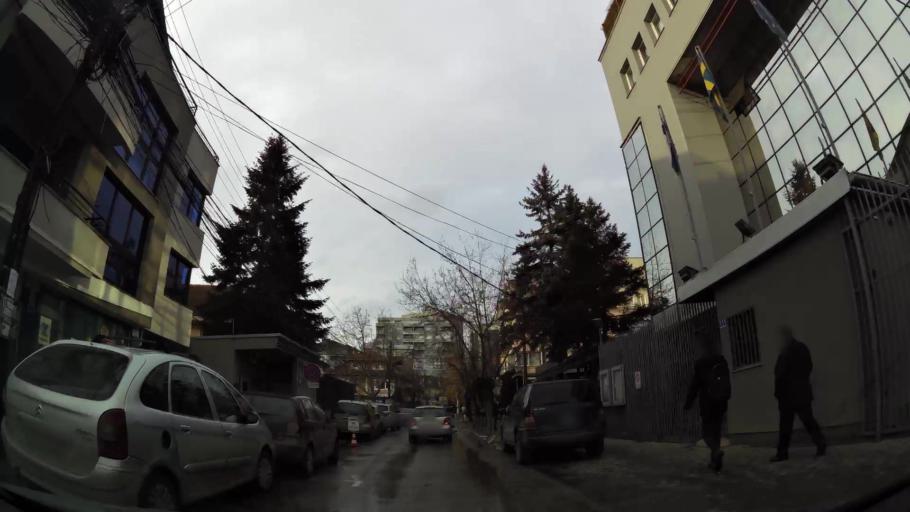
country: XK
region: Pristina
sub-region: Komuna e Prishtines
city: Pristina
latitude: 42.6569
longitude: 21.1574
